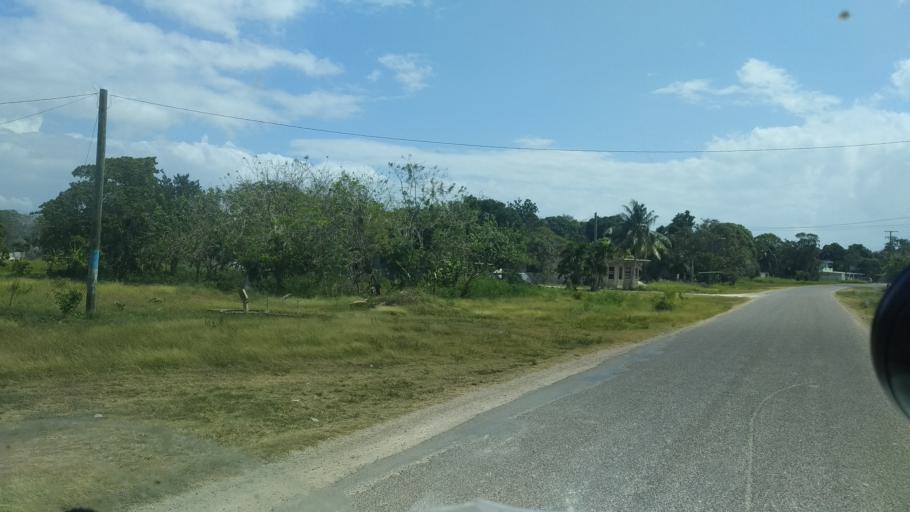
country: BZ
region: Corozal
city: Corozal
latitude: 18.3902
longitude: -88.4173
